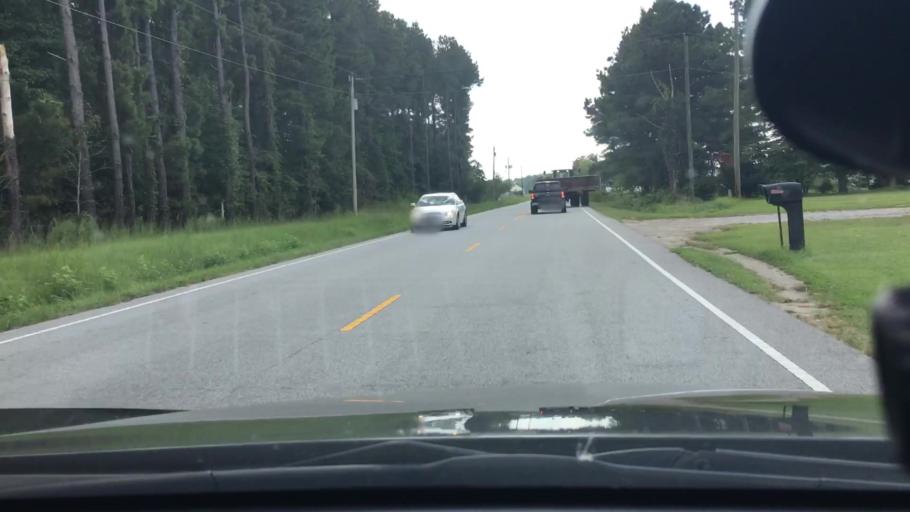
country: US
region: North Carolina
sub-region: Pitt County
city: Farmville
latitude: 35.7139
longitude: -77.5235
